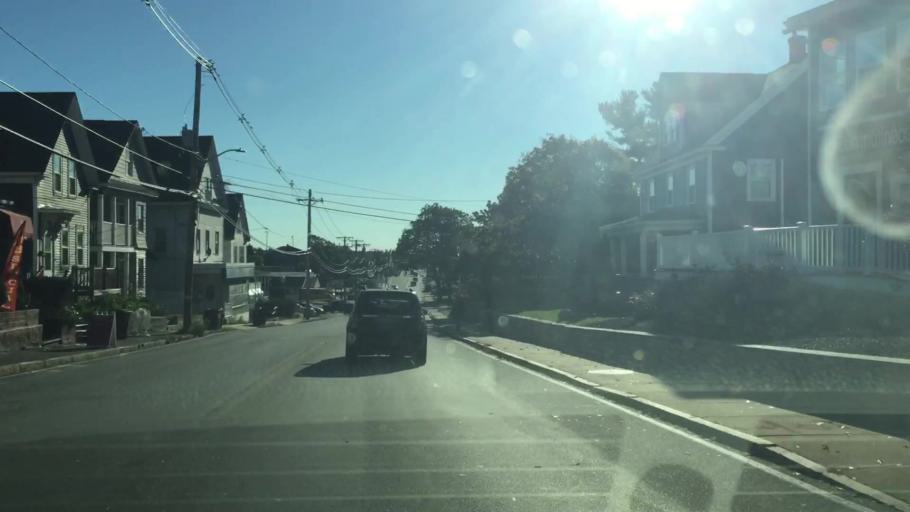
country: US
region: Massachusetts
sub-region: Middlesex County
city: Lowell
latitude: 42.6334
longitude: -71.2901
